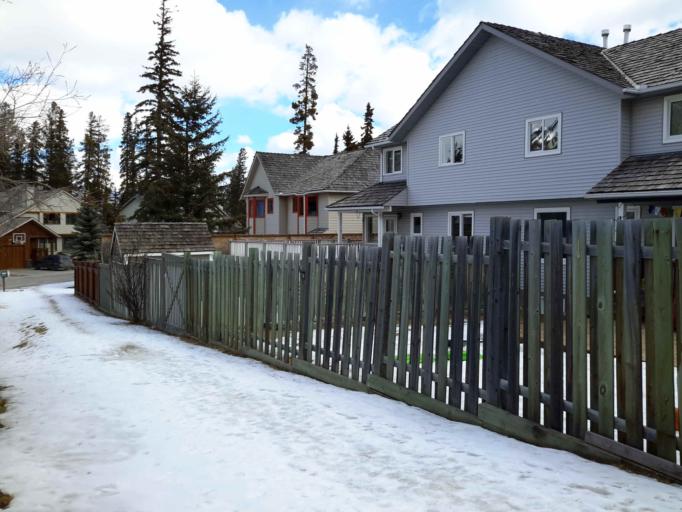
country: CA
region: Alberta
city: Banff
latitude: 51.1685
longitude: -115.5769
